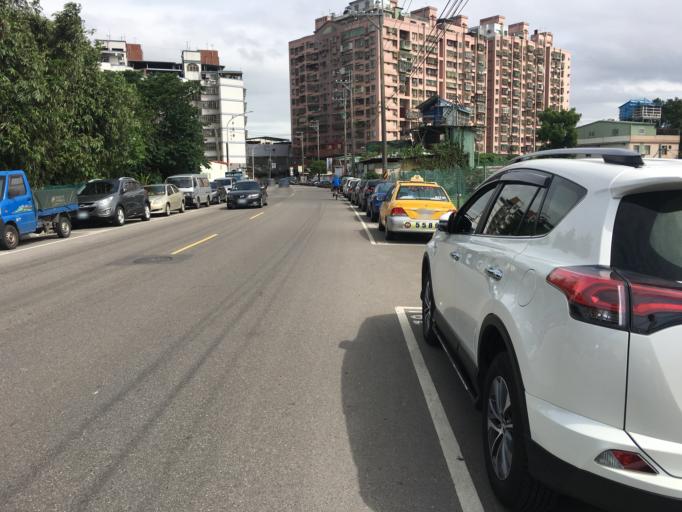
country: TW
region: Taipei
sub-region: Taipei
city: Banqiao
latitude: 24.9768
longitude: 121.4214
